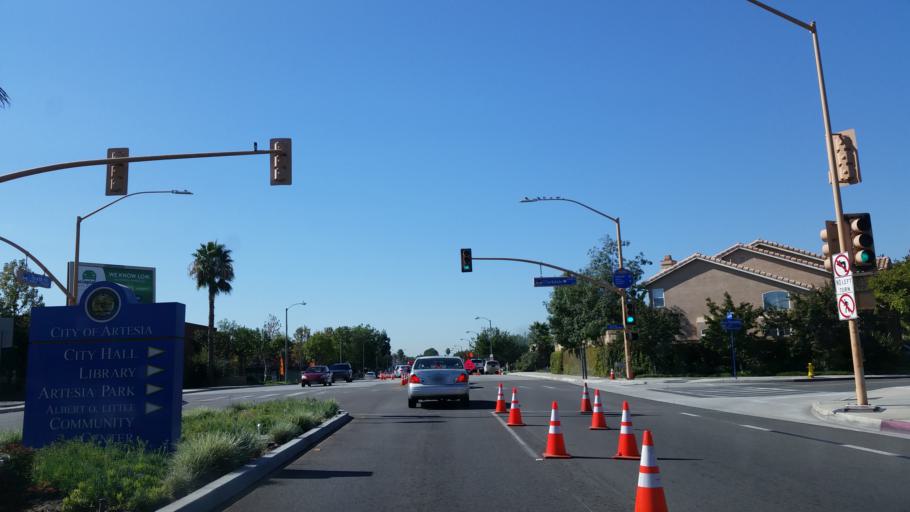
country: US
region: California
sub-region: Los Angeles County
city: Artesia
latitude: 33.8585
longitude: -118.0783
